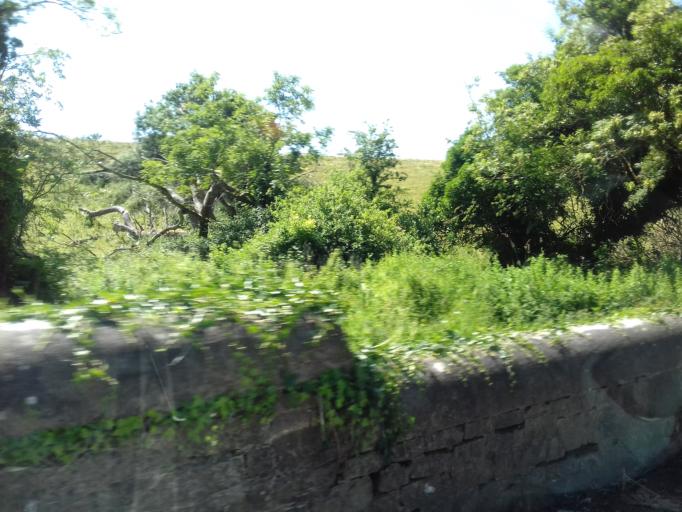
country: IE
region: Leinster
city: Ballymun
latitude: 53.4552
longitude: -6.2767
